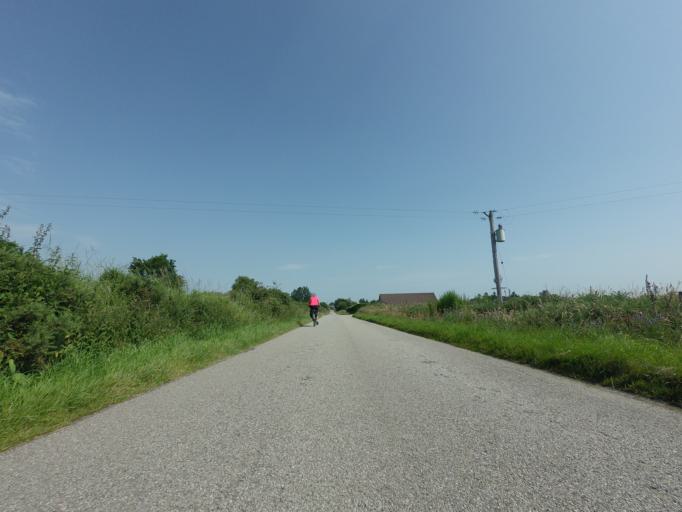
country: GB
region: Scotland
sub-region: Highland
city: Tain
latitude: 57.7993
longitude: -4.0685
